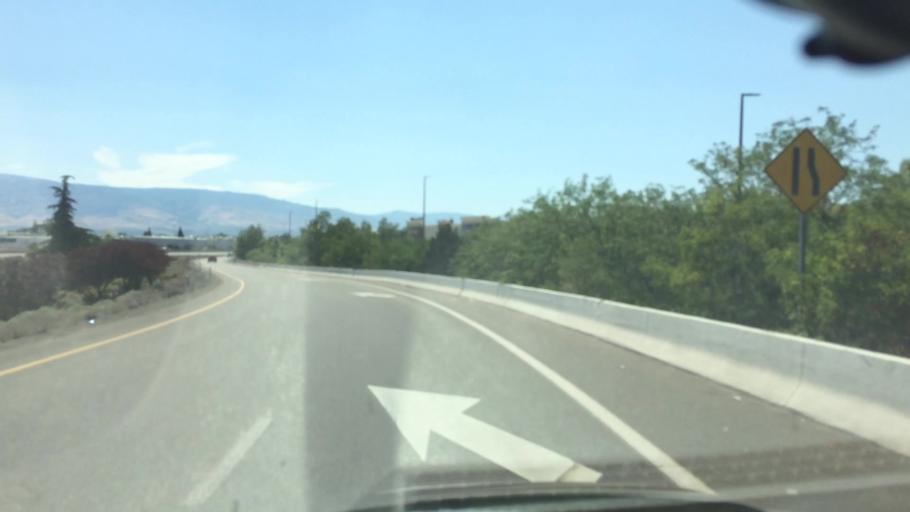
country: US
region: Nevada
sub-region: Washoe County
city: Sparks
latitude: 39.5299
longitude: -119.7162
